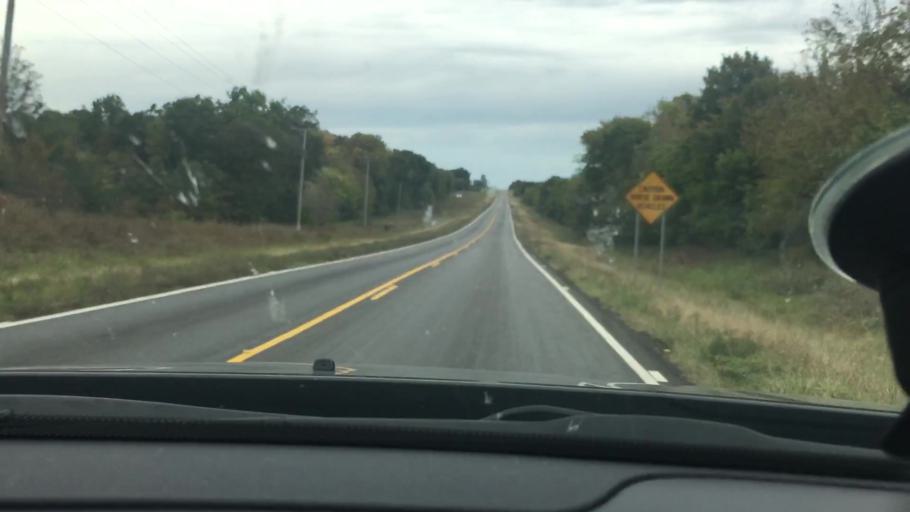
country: US
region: Oklahoma
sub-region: Coal County
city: Coalgate
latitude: 34.3795
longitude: -96.4245
